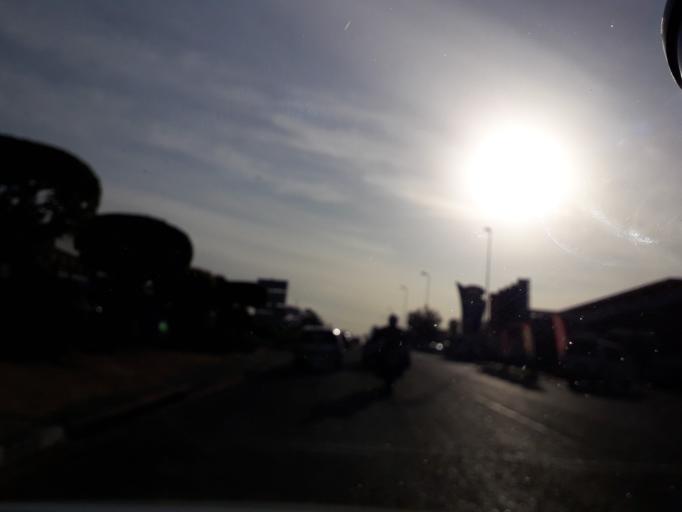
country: ZA
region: Gauteng
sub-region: City of Johannesburg Metropolitan Municipality
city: Johannesburg
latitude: -26.0819
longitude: 27.9841
